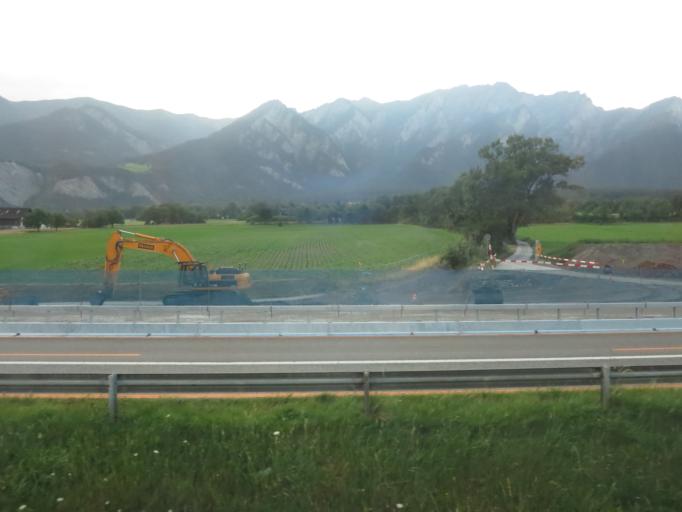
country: CH
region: Grisons
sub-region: Landquart District
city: Trimmis
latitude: 46.8950
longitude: 9.5416
